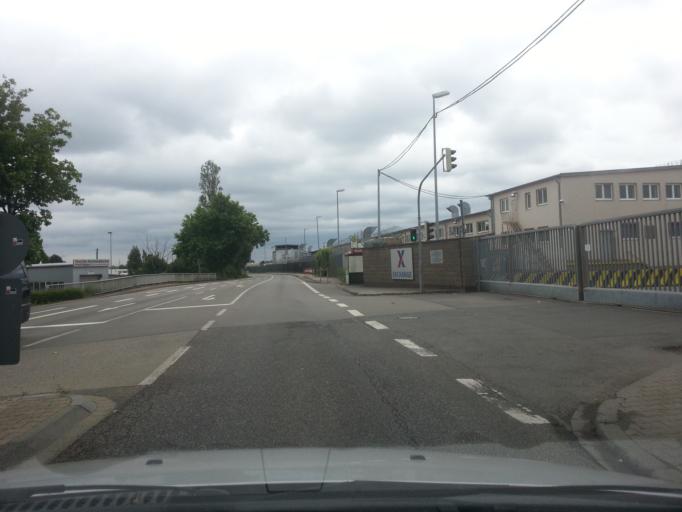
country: DE
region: Rheinland-Pfalz
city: Grunstadt
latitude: 49.5554
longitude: 8.1769
